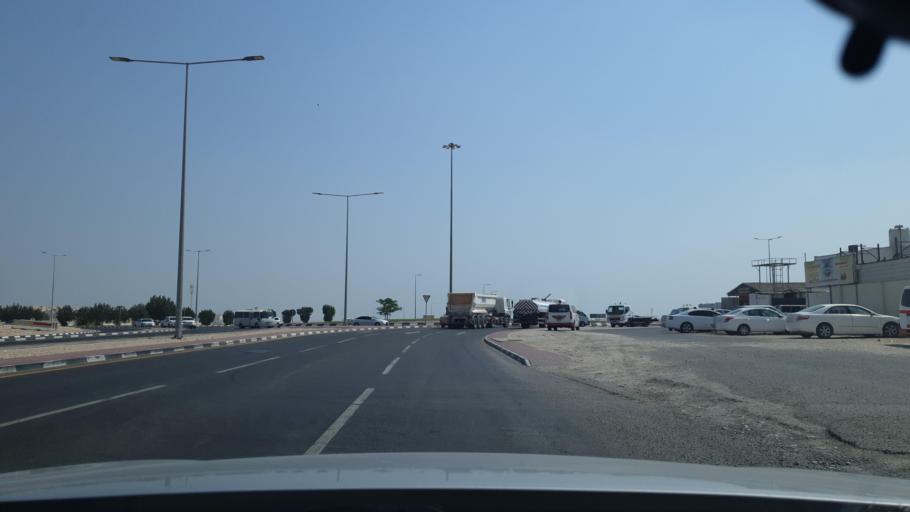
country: QA
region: Al Khawr
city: Al Khawr
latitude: 25.7145
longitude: 51.5080
